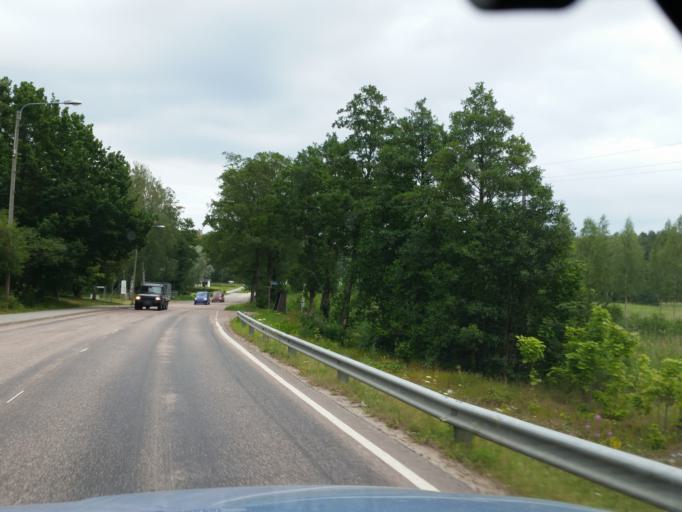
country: FI
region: Varsinais-Suomi
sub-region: Aboland-Turunmaa
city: Nagu
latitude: 60.1915
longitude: 21.9156
